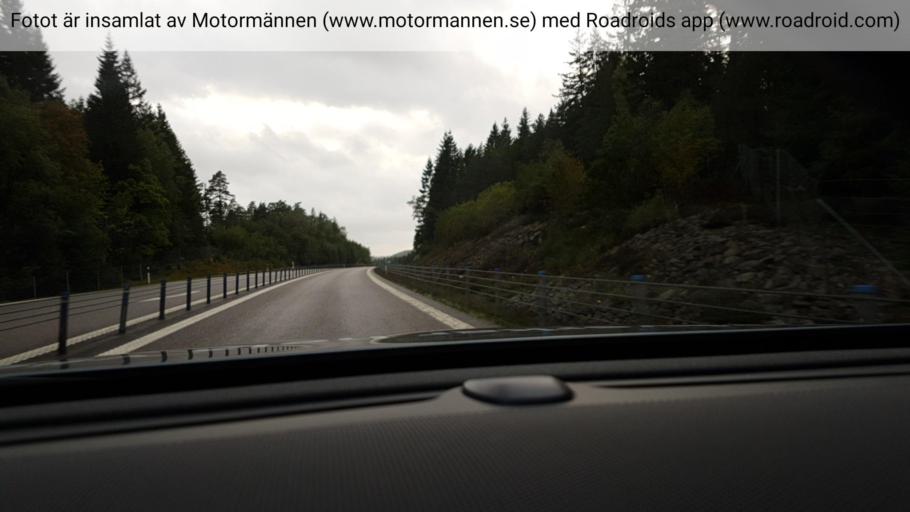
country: SE
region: Vaestra Goetaland
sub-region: Uddevalla Kommun
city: Uddevalla
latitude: 58.3250
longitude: 11.9617
